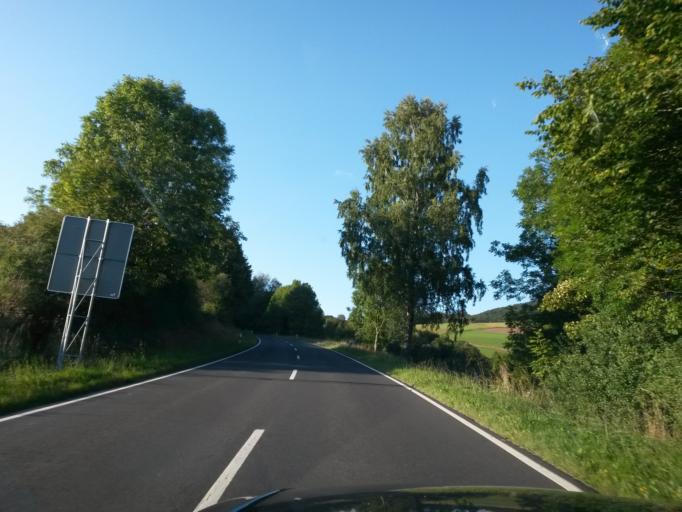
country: DE
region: Hesse
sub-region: Regierungsbezirk Kassel
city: Gersfeld
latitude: 50.4577
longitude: 9.9379
